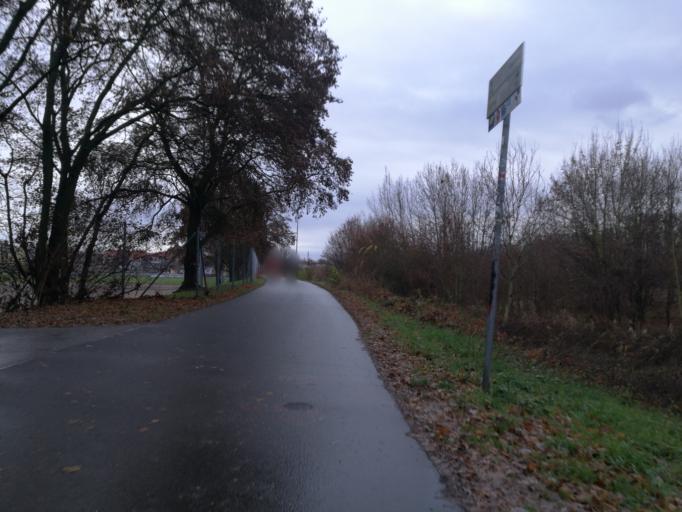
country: DE
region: Bavaria
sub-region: Regierungsbezirk Mittelfranken
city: Wetzendorf
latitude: 49.4680
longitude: 11.0203
